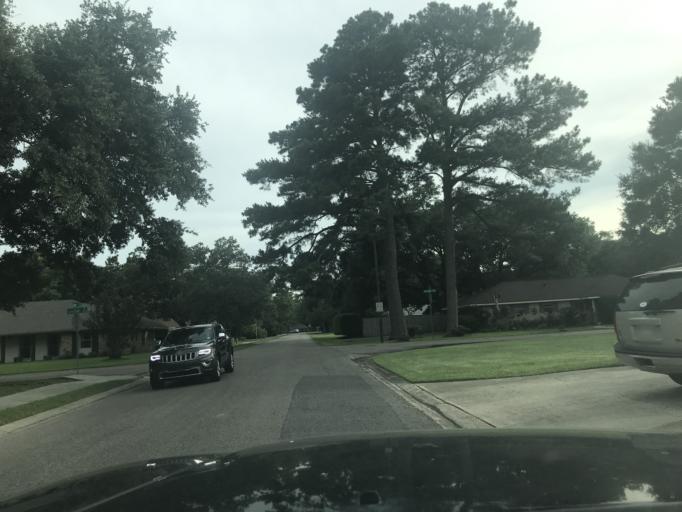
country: US
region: Louisiana
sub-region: Lafayette Parish
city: Lafayette
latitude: 30.1939
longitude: -92.0467
